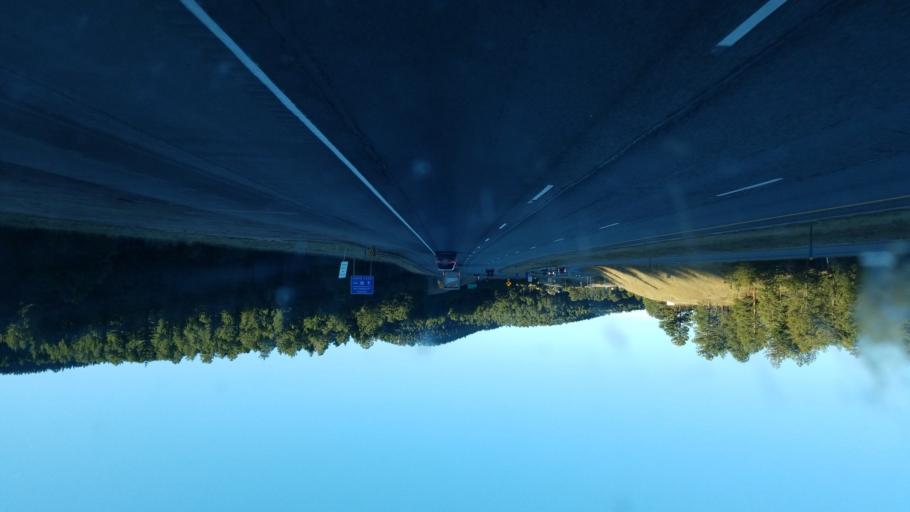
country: US
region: Colorado
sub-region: Jefferson County
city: Kittredge
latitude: 39.7070
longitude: -105.3465
